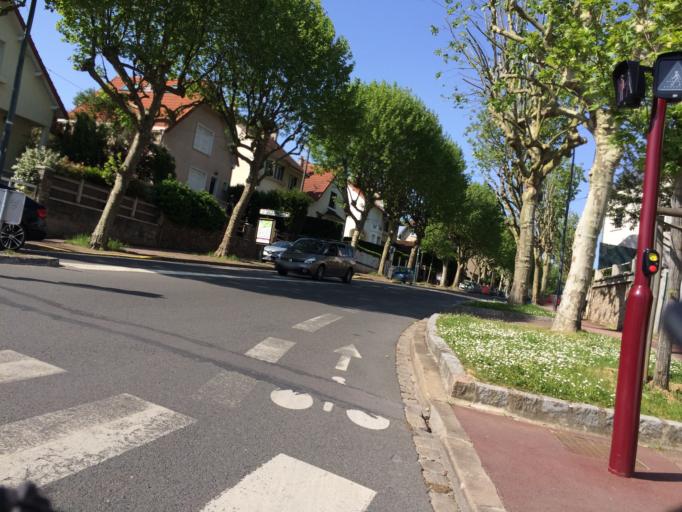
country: FR
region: Ile-de-France
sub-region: Departement des Hauts-de-Seine
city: Sceaux
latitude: 48.7765
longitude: 2.2784
